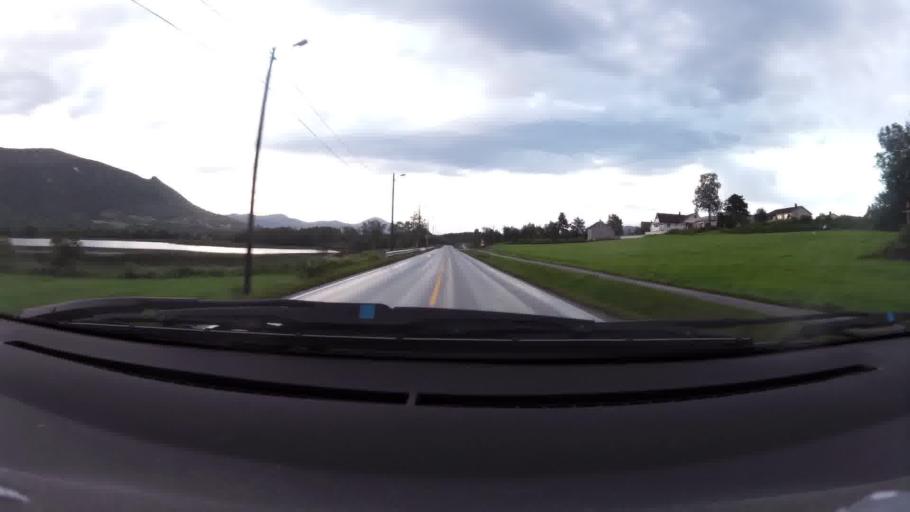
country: NO
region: More og Romsdal
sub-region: Eide
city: Eide
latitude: 62.8959
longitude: 7.4078
